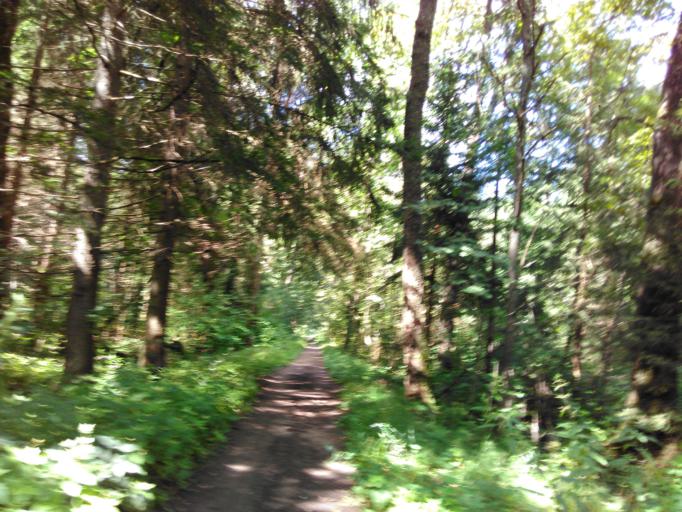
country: RU
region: Tverskaya
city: Konakovo
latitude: 56.6847
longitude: 36.7066
